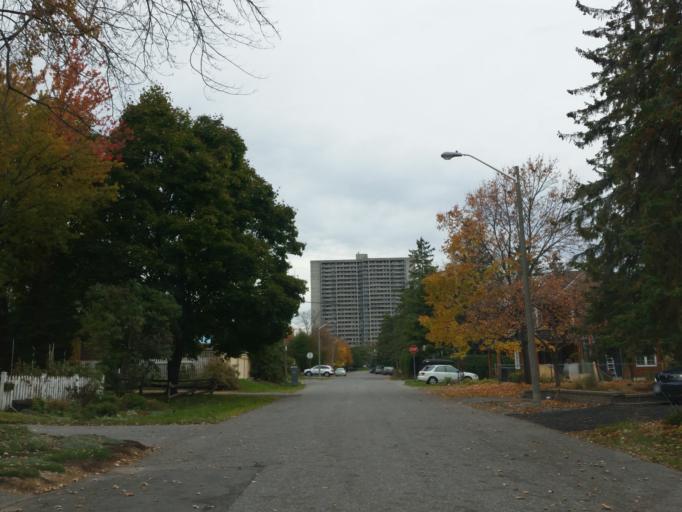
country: CA
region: Ontario
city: Bells Corners
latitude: 45.3640
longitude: -75.7965
